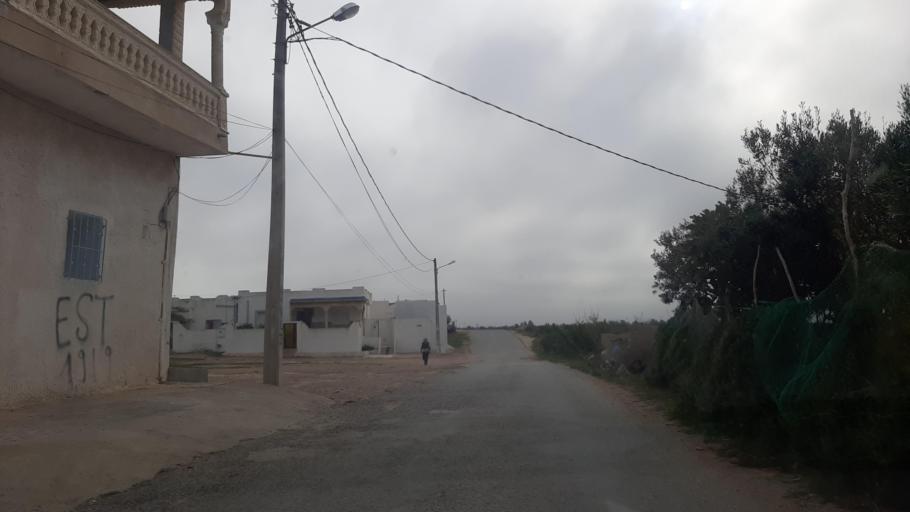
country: TN
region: Nabul
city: Menzel Heurr
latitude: 36.6750
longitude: 10.9215
